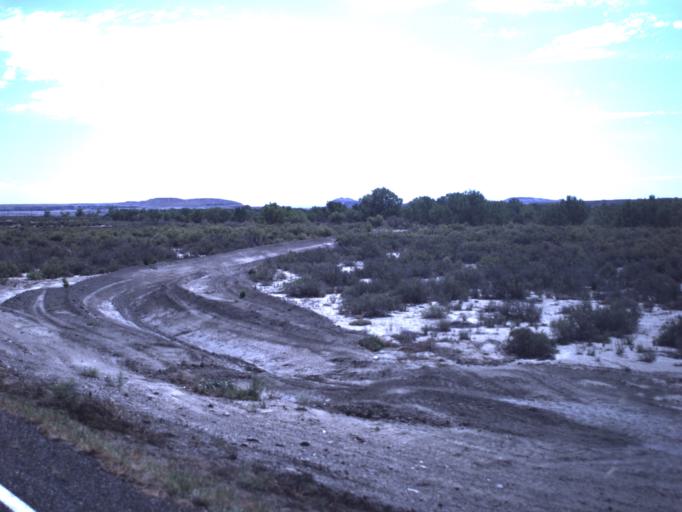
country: US
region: Utah
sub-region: Emery County
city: Ferron
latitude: 38.3670
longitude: -110.8549
